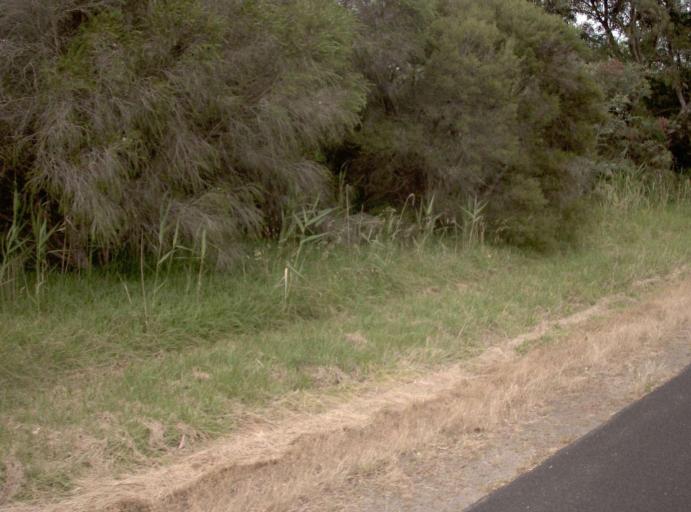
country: AU
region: Victoria
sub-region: East Gippsland
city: Bairnsdale
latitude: -37.8716
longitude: 147.6506
